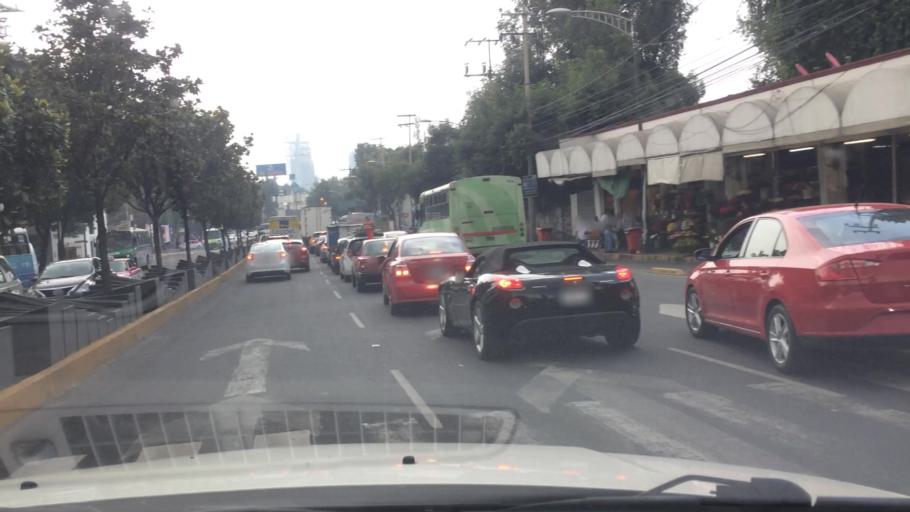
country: MX
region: Mexico City
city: Alvaro Obregon
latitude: 19.3473
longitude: -99.1903
